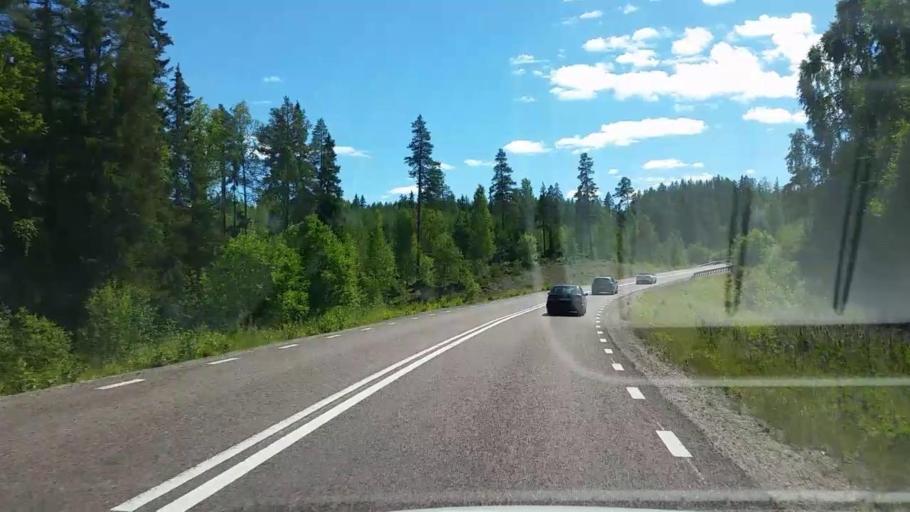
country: SE
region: Gaevleborg
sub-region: Ovanakers Kommun
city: Edsbyn
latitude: 61.2305
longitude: 15.8844
